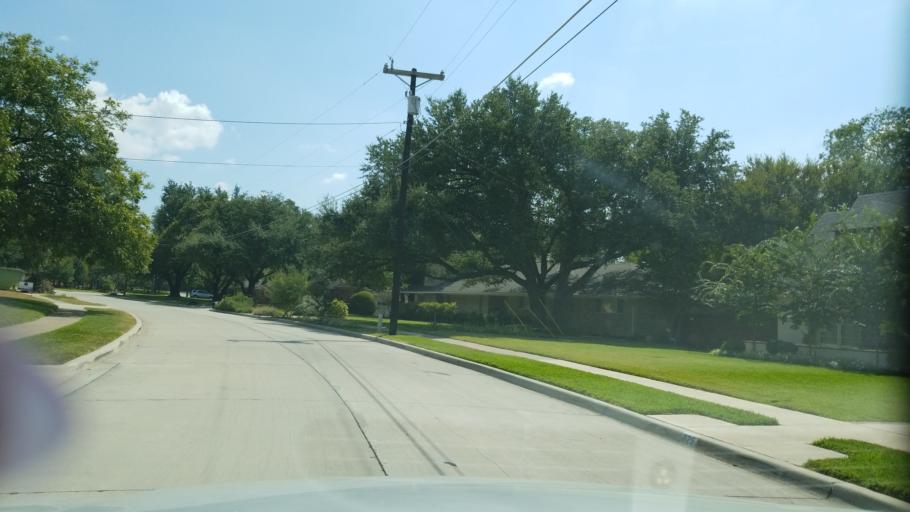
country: US
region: Texas
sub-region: Dallas County
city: Richardson
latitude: 32.9534
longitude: -96.7513
